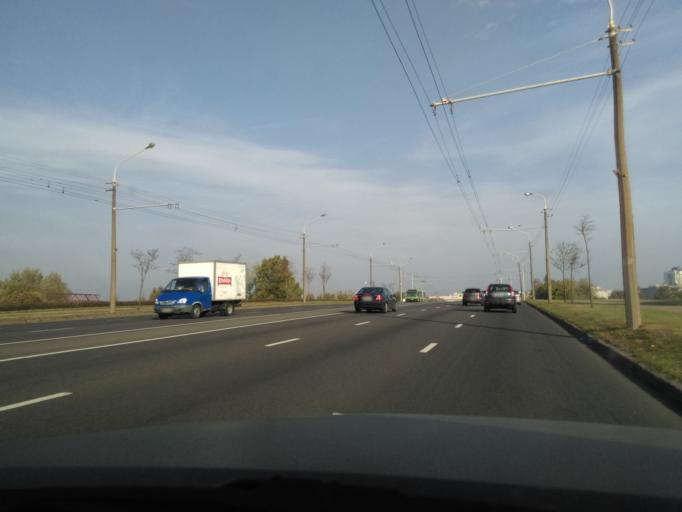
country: BY
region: Minsk
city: Minsk
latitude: 53.9023
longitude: 27.6374
